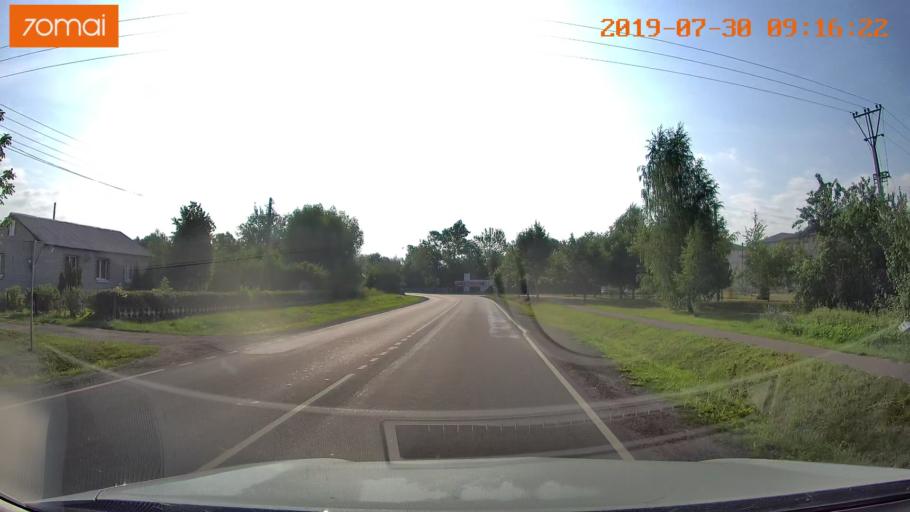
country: RU
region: Kaliningrad
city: Nesterov
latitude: 54.6338
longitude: 22.5569
